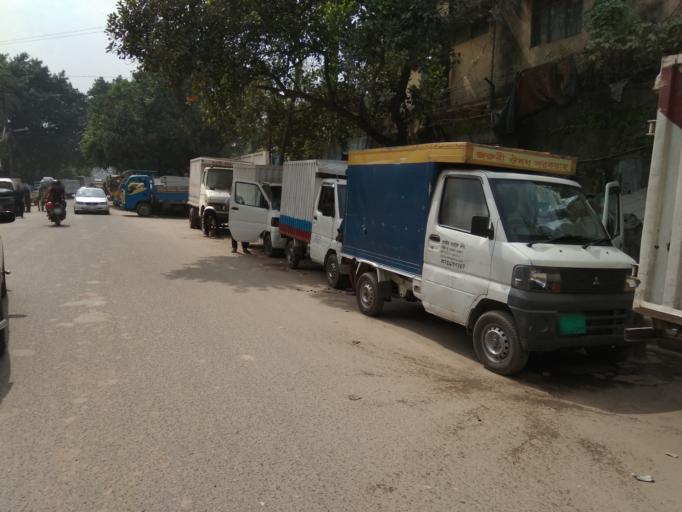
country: BD
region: Dhaka
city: Paltan
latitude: 23.7693
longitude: 90.4031
